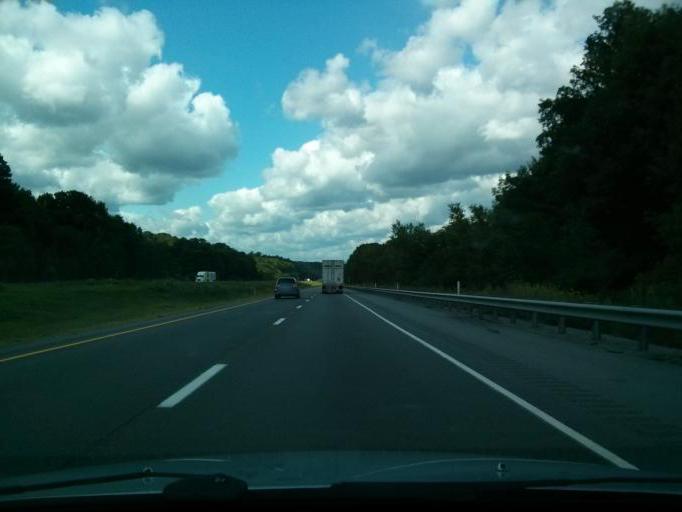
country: US
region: Pennsylvania
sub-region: Clearfield County
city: Treasure Lake
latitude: 41.1219
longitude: -78.6591
